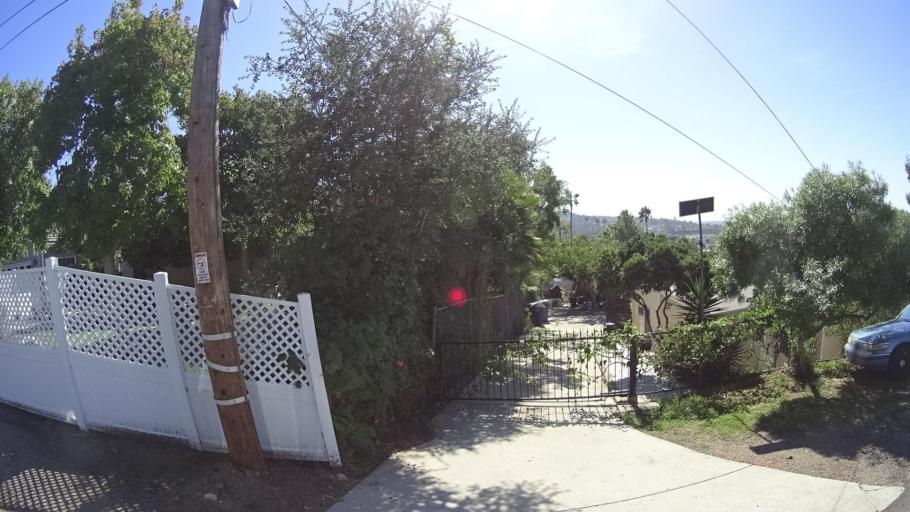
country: US
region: California
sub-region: San Diego County
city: Casa de Oro-Mount Helix
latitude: 32.7531
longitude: -116.9810
